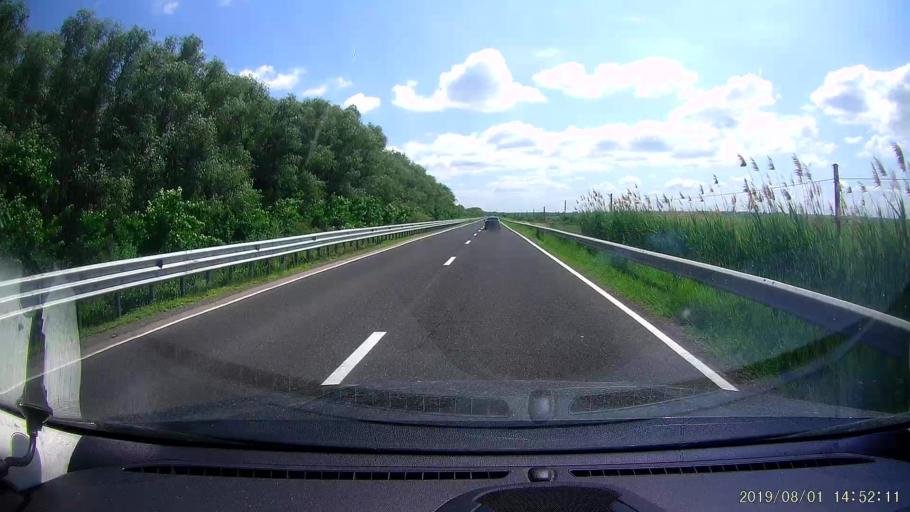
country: RO
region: Braila
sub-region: Comuna Vadeni
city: Vadeni
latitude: 45.3603
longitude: 28.0124
